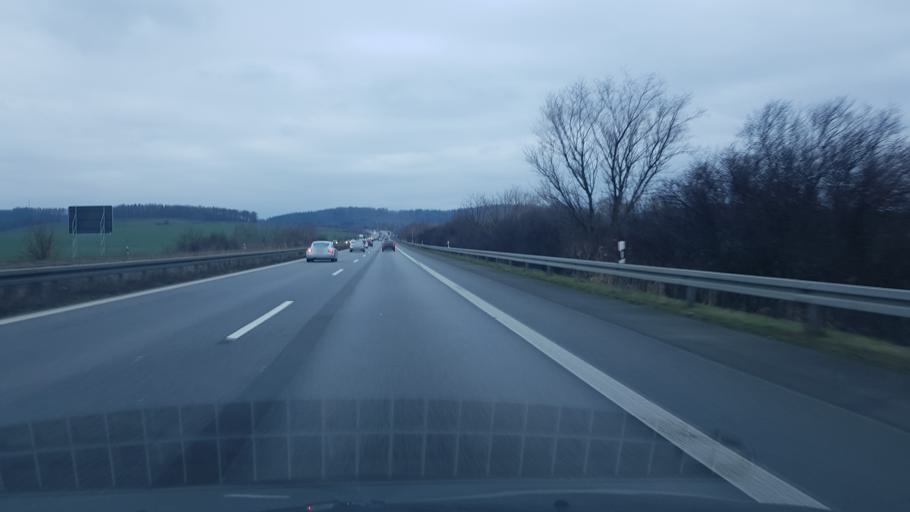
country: DE
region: Saxony
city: Burkau
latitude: 51.1835
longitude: 14.1657
